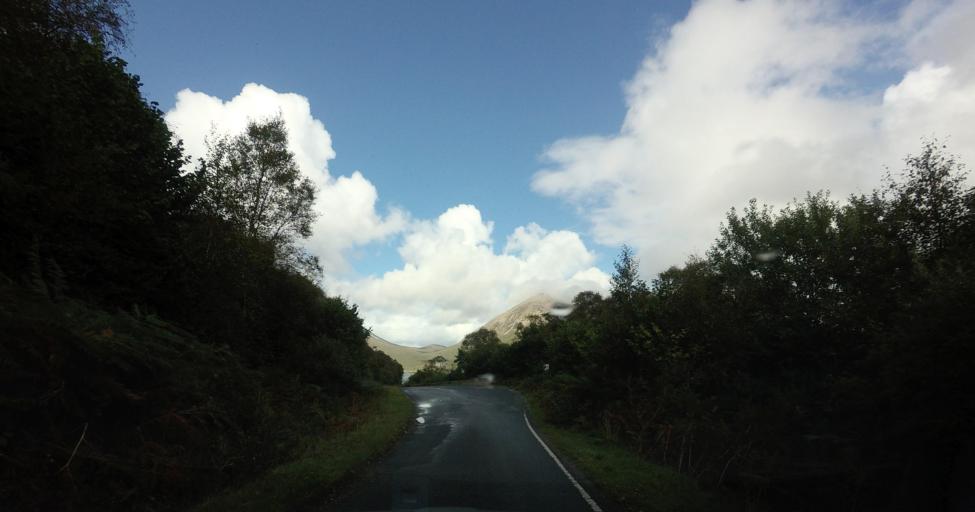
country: GB
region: Scotland
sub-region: Highland
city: Portree
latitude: 57.1992
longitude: -6.0274
